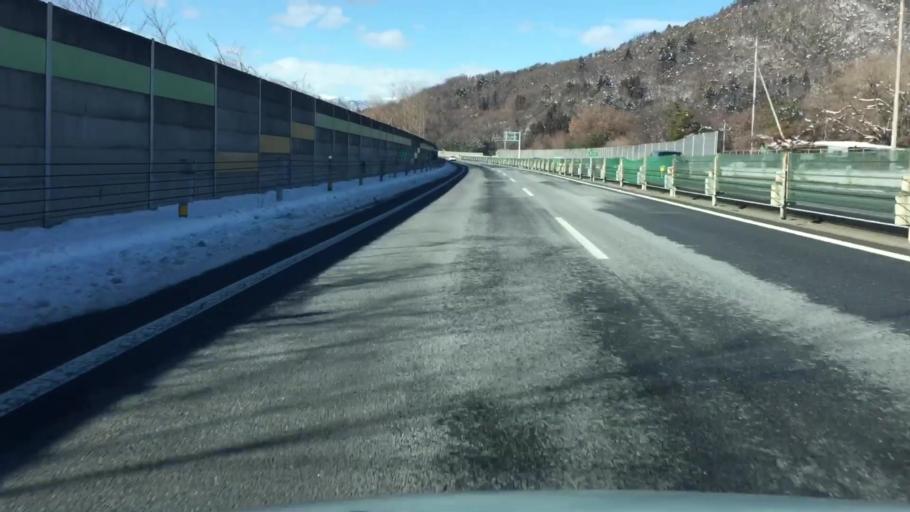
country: JP
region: Gunma
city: Numata
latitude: 36.6712
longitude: 139.0448
